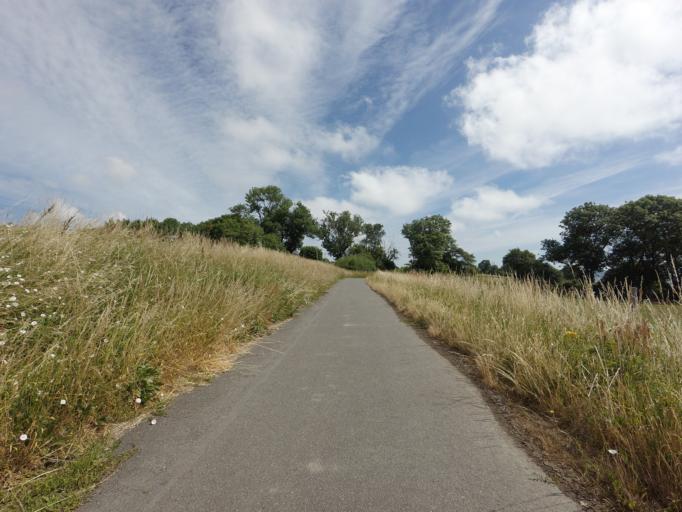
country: SE
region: Skane
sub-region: Simrishamns Kommun
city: Simrishamn
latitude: 55.5041
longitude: 14.3288
